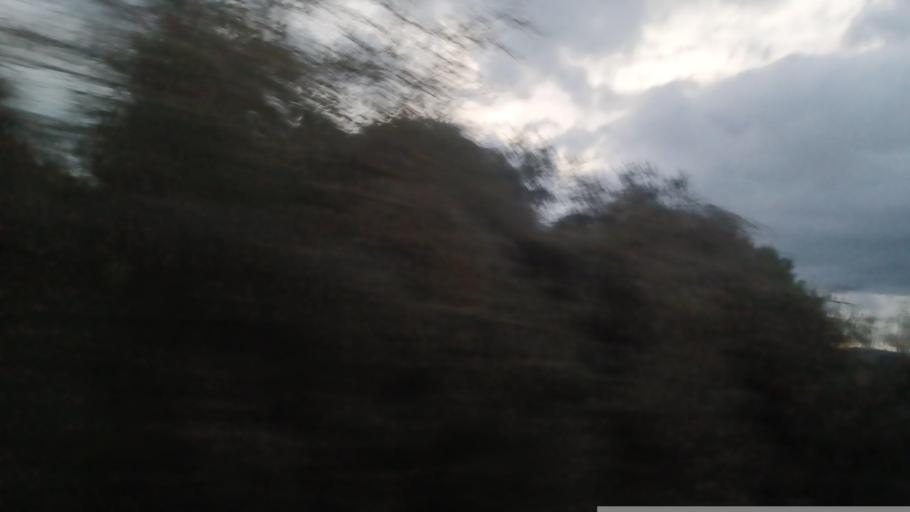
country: CY
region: Pafos
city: Mesogi
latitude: 34.8593
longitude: 32.5502
